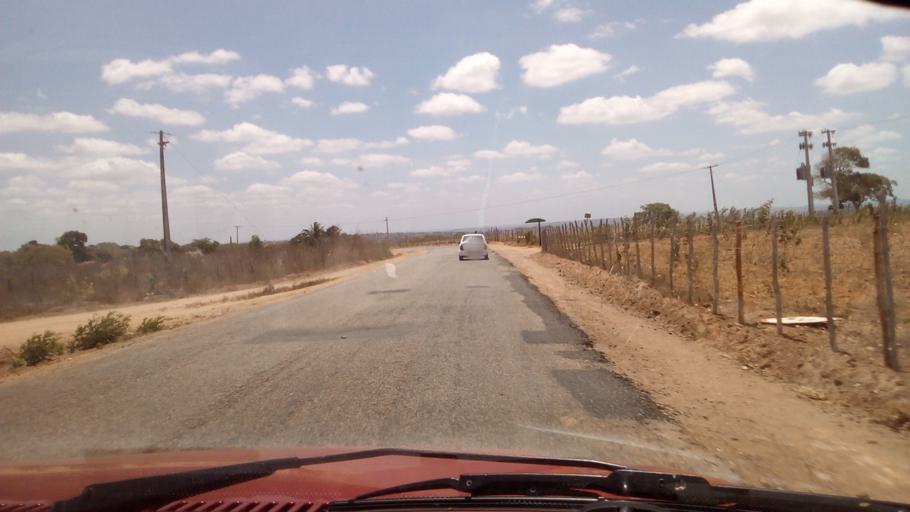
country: BR
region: Paraiba
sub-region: Cacimba De Dentro
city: Cacimba de Dentro
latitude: -6.5967
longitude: -35.8141
